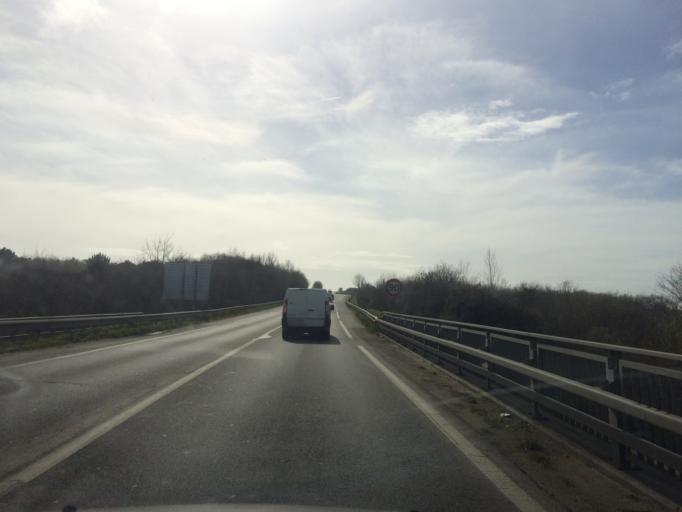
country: FR
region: Pays de la Loire
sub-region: Departement de la Loire-Atlantique
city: Saint-Nazaire
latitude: 47.2844
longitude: -2.2495
